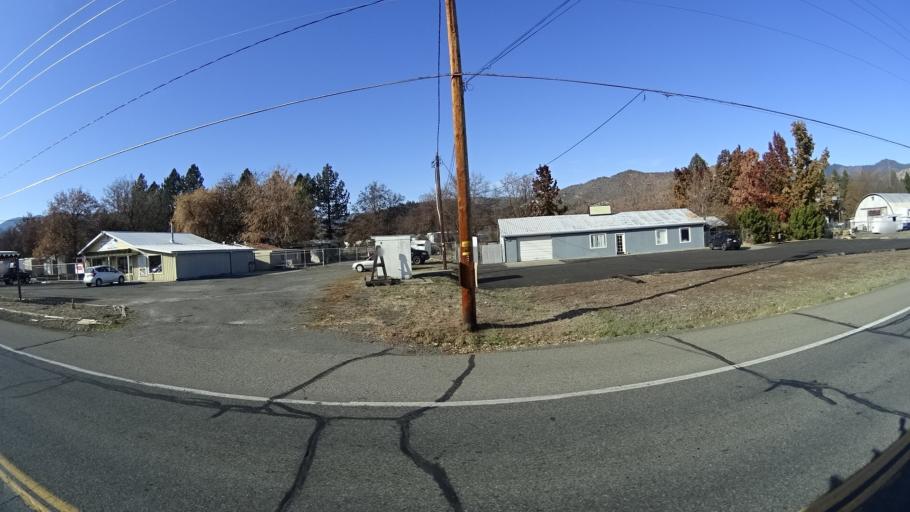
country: US
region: California
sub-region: Siskiyou County
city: Yreka
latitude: 41.6998
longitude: -122.6399
